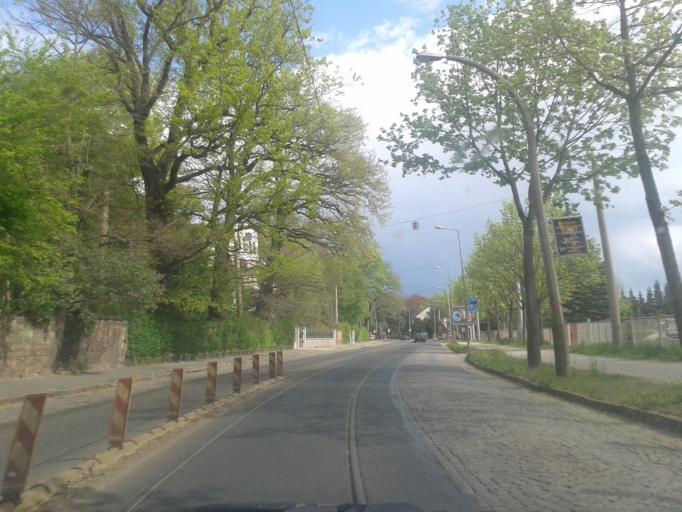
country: DE
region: Saxony
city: Radebeul
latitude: 51.1061
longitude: 13.6493
